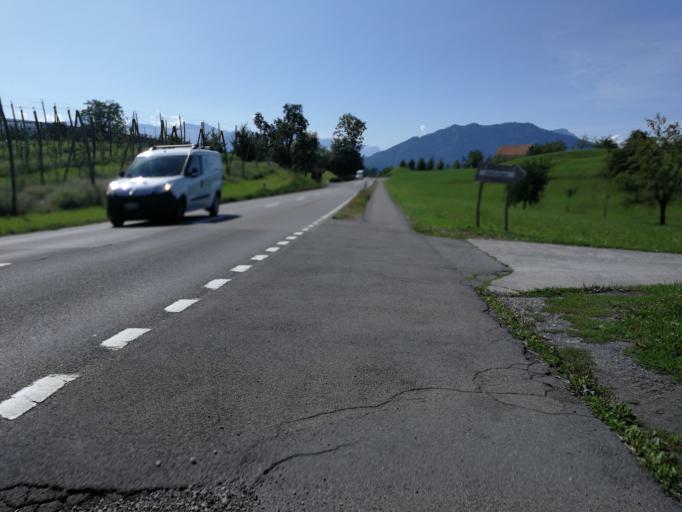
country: CH
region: Lucerne
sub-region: Lucerne-Land District
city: Weggis
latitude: 47.0483
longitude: 8.4260
